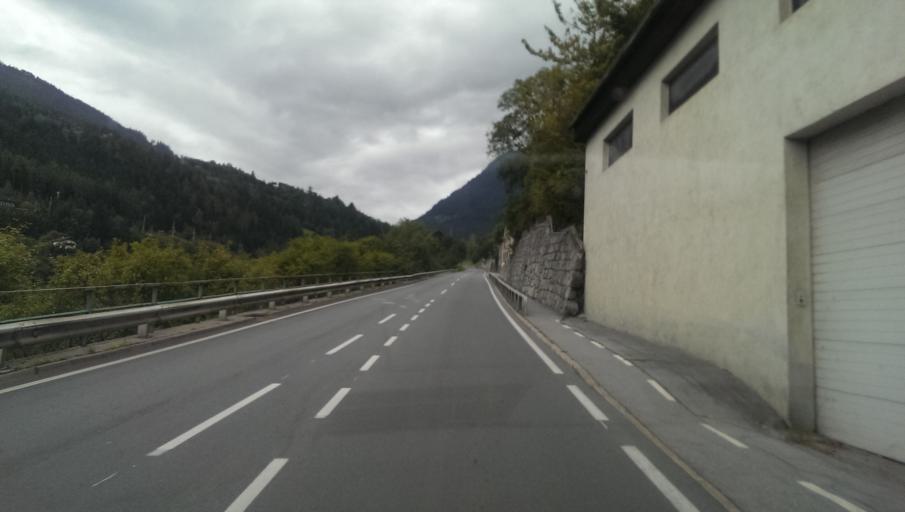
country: AT
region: Tyrol
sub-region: Politischer Bezirk Landeck
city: Pians
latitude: 47.1346
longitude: 10.5106
